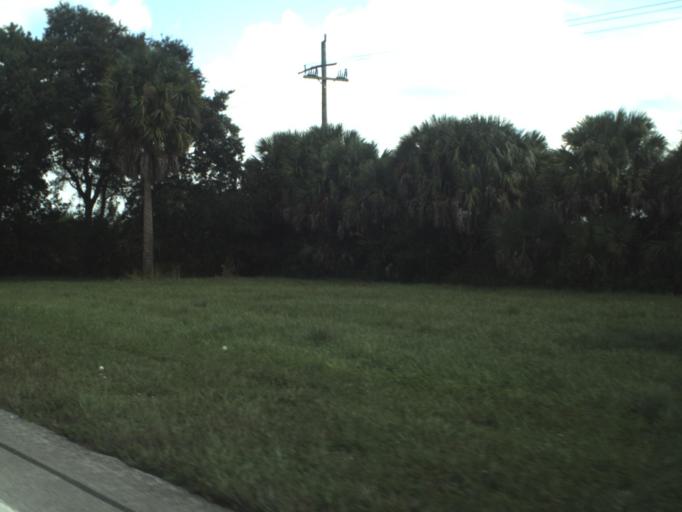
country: US
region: Florida
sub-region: Martin County
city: Indiantown
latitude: 27.0000
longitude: -80.4370
